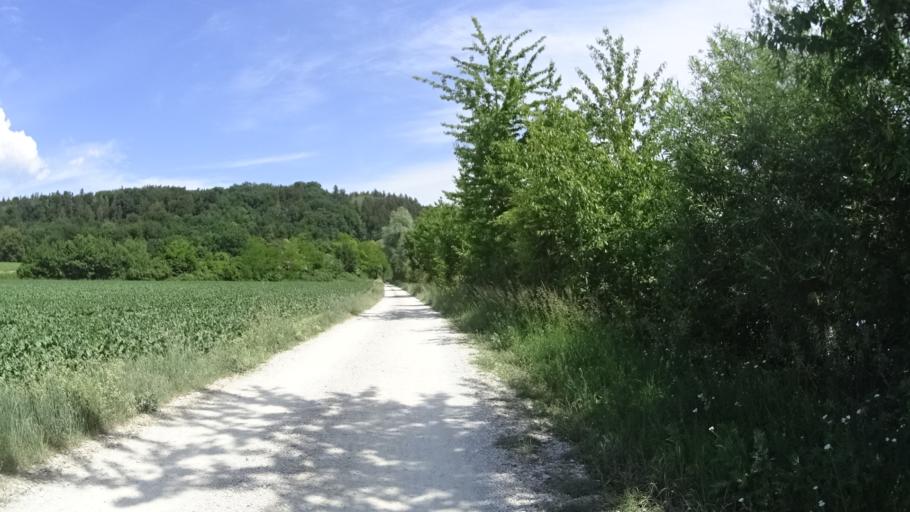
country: DE
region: Bavaria
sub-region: Lower Bavaria
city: Saal
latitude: 48.9187
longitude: 11.9698
